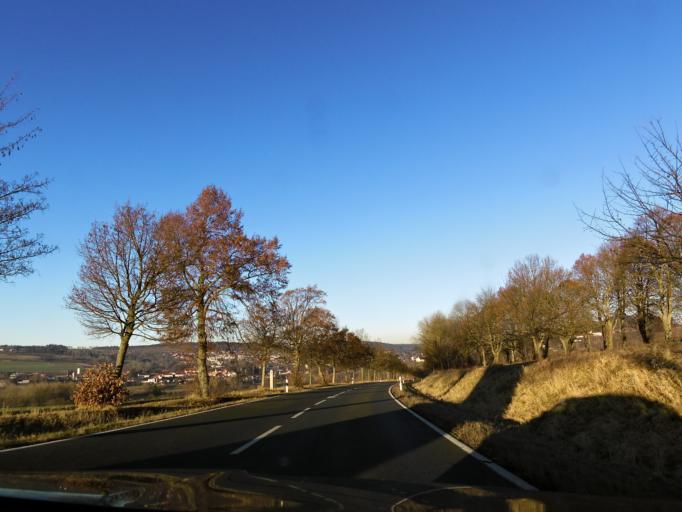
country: DE
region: Bavaria
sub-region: Upper Franconia
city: Wunsiedel
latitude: 50.0239
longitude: 11.9965
